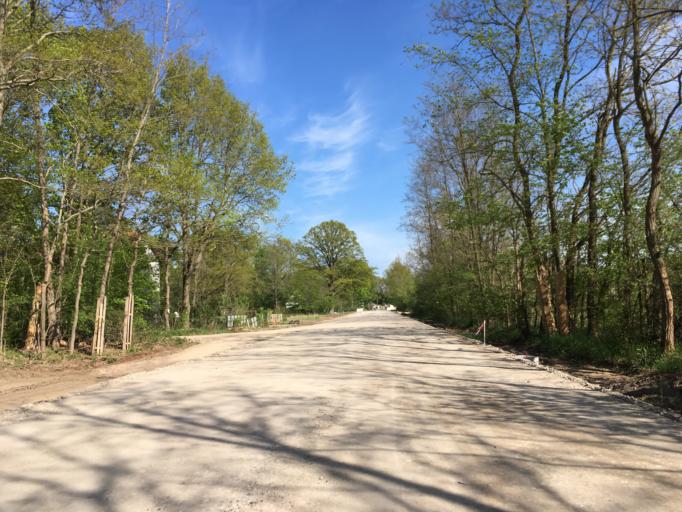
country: DE
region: Brandenburg
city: Rudnitz
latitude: 52.7253
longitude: 13.6112
